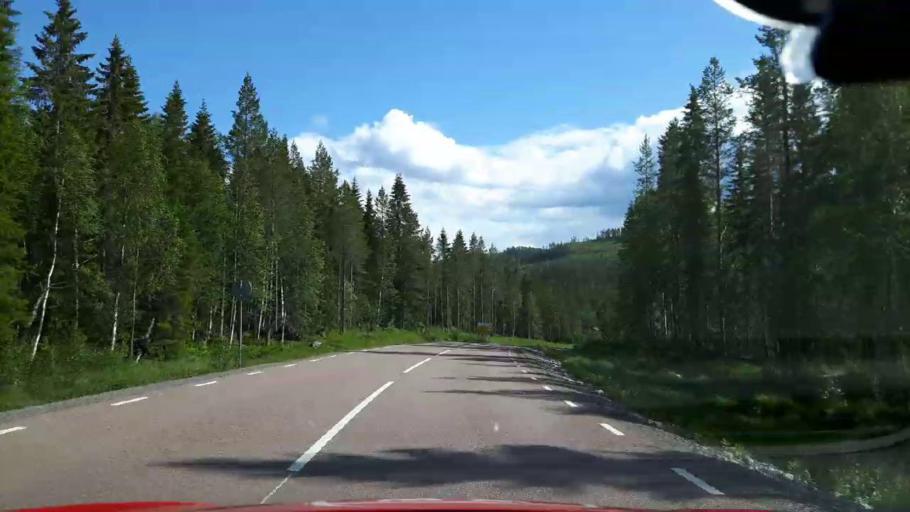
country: SE
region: Jaemtland
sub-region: Krokoms Kommun
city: Valla
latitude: 64.0206
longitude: 14.2071
